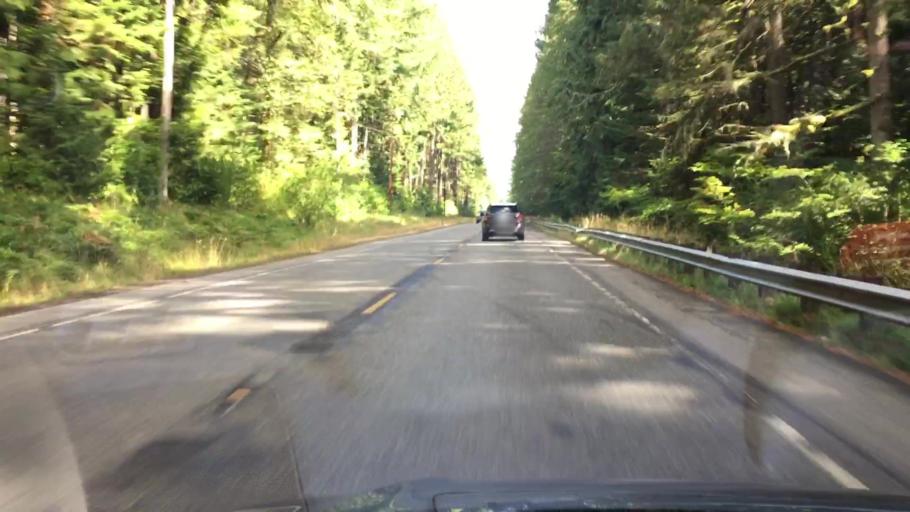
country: US
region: Washington
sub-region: Pierce County
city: Eatonville
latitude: 46.7563
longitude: -122.0804
